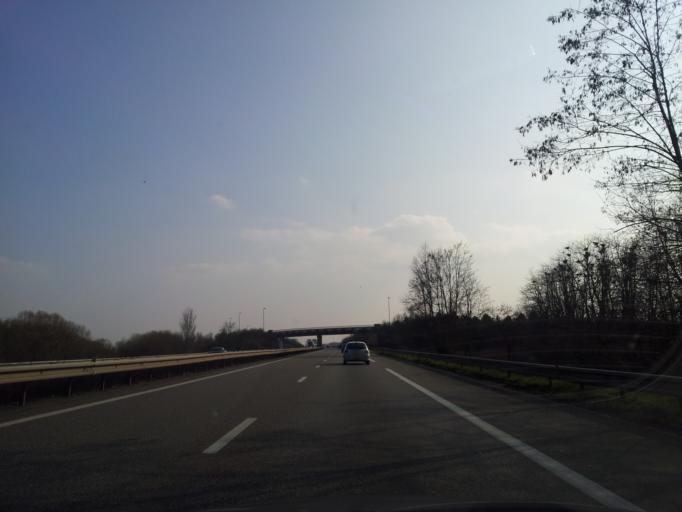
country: FR
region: Alsace
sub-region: Departement du Haut-Rhin
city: Horbourg-Wihr
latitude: 48.0989
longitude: 7.3822
